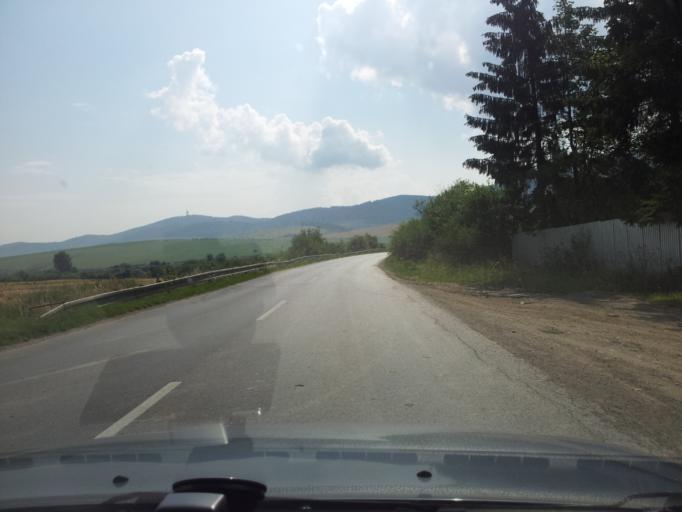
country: SK
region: Zilinsky
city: Namestovo
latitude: 49.3725
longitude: 19.4100
